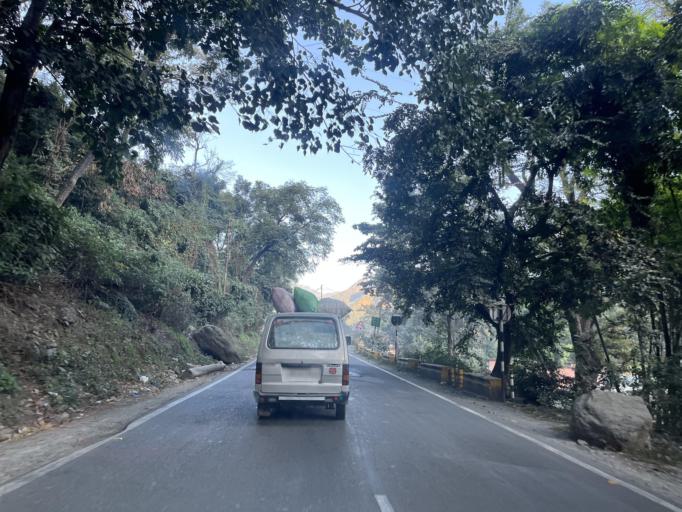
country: IN
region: Uttarakhand
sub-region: Naini Tal
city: Bhim Tal
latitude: 29.2898
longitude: 79.5463
